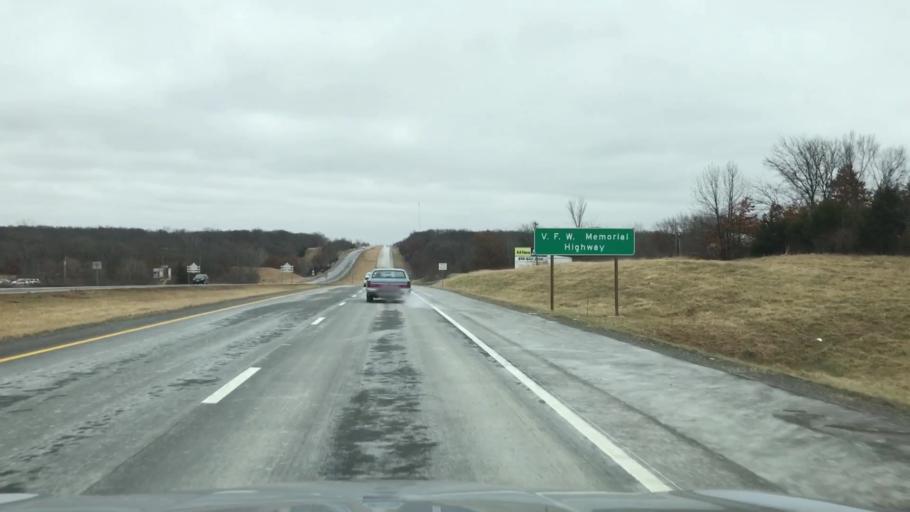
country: US
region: Missouri
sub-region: Clinton County
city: Cameron
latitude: 39.7532
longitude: -94.2117
